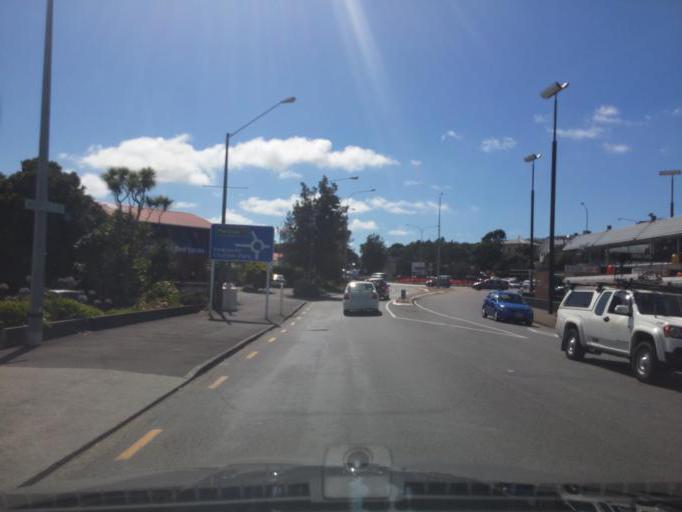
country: NZ
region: Wellington
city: Petone
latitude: -41.2219
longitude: 174.8064
